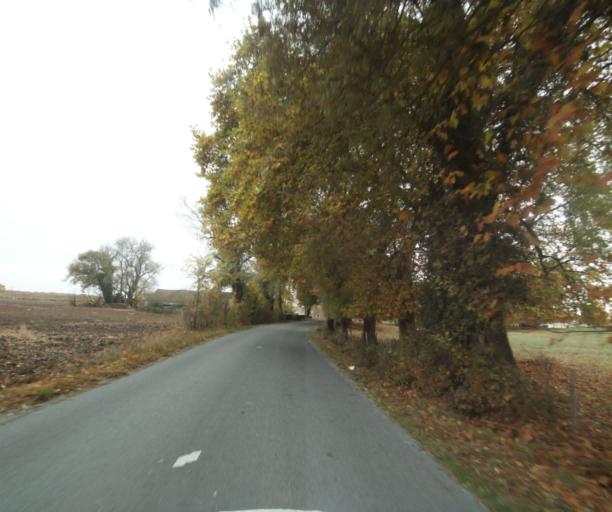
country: FR
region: Poitou-Charentes
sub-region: Departement de la Charente-Maritime
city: Chermignac
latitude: 45.7167
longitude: -0.6764
